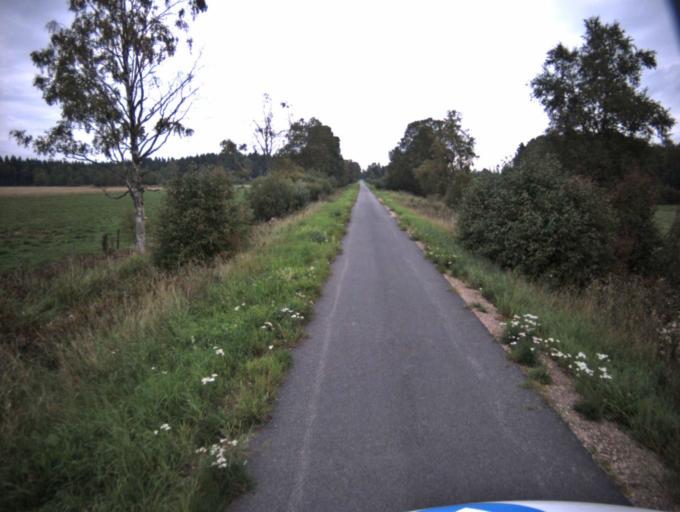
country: SE
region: Vaestra Goetaland
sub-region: Falkopings Kommun
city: Falkoeping
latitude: 58.0012
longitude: 13.5466
